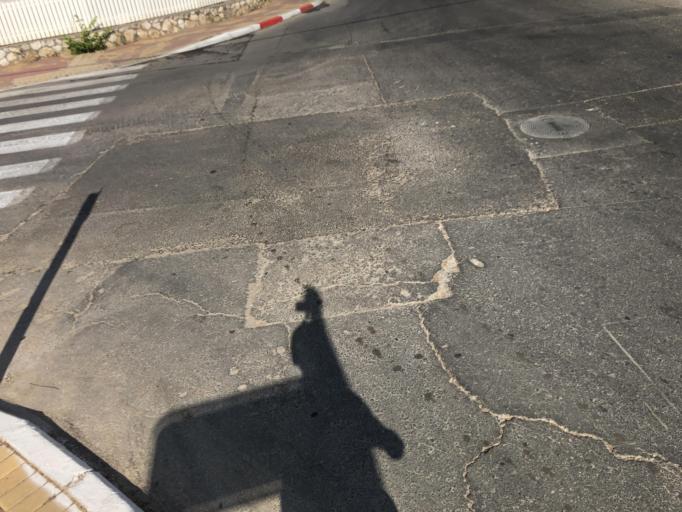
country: IL
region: Central District
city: Yehud
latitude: 32.0344
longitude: 34.8964
